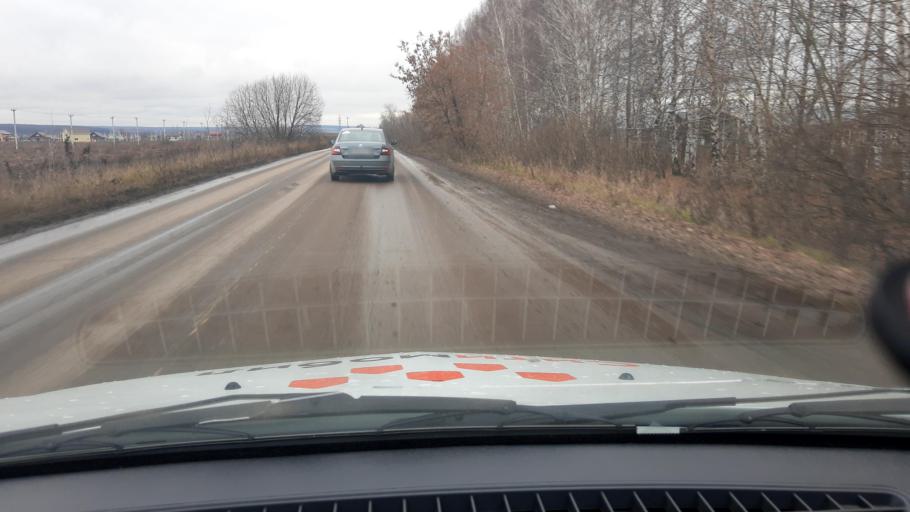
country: RU
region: Bashkortostan
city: Kabakovo
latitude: 54.6750
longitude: 56.1412
